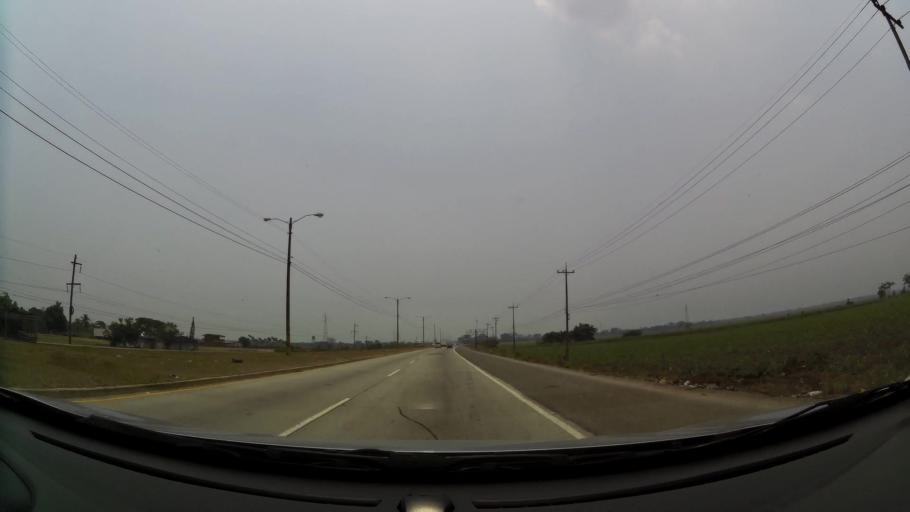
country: HN
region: Cortes
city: La Lima
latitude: 15.4118
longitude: -87.8610
